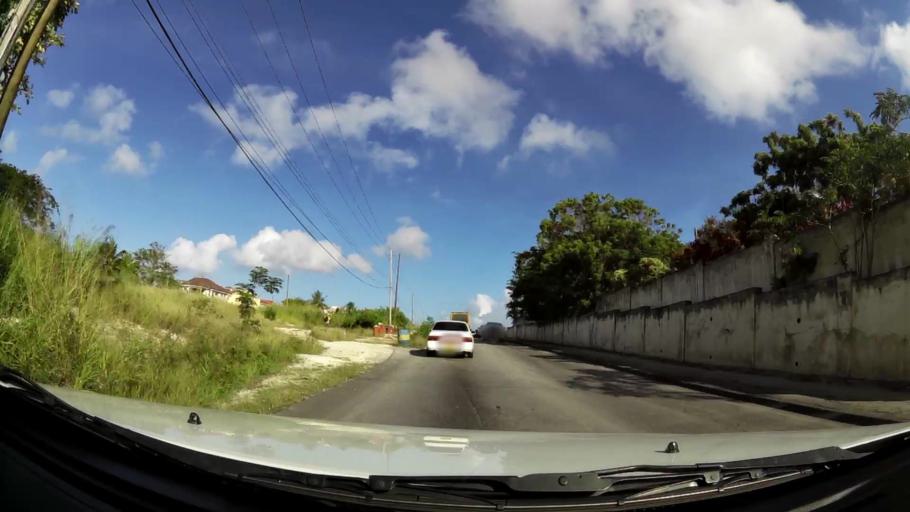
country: BB
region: Saint James
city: Holetown
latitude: 13.1488
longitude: -59.6113
